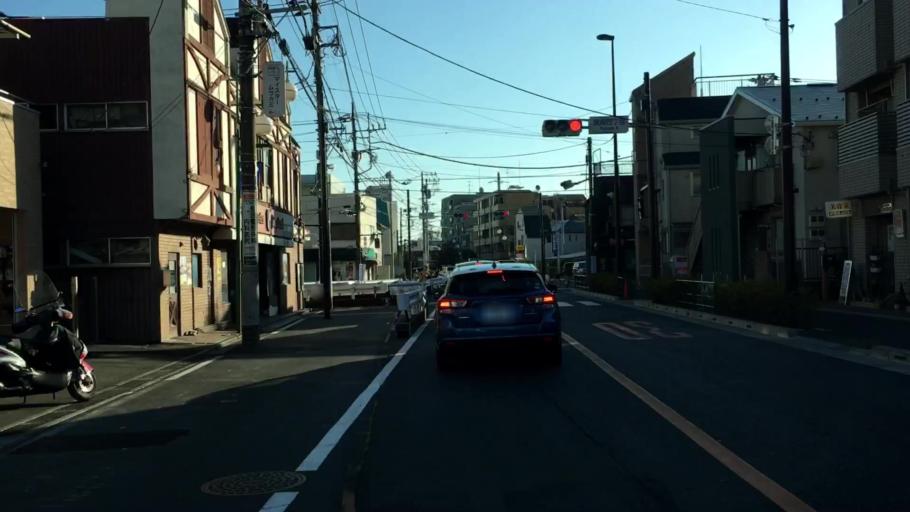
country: JP
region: Tokyo
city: Kamirenjaku
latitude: 35.6985
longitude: 139.5381
